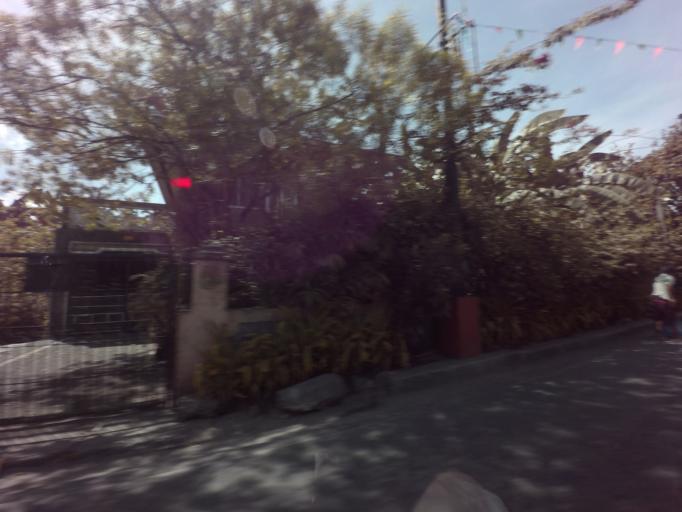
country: PH
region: Calabarzon
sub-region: Province of Rizal
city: Taguig
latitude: 14.5318
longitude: 121.0774
